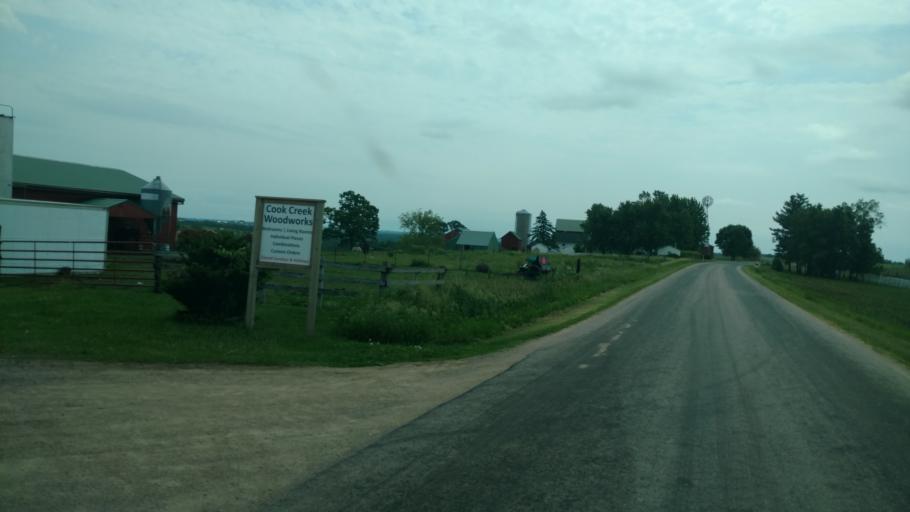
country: US
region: Wisconsin
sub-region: Monroe County
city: Cashton
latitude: 43.7717
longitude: -90.6614
